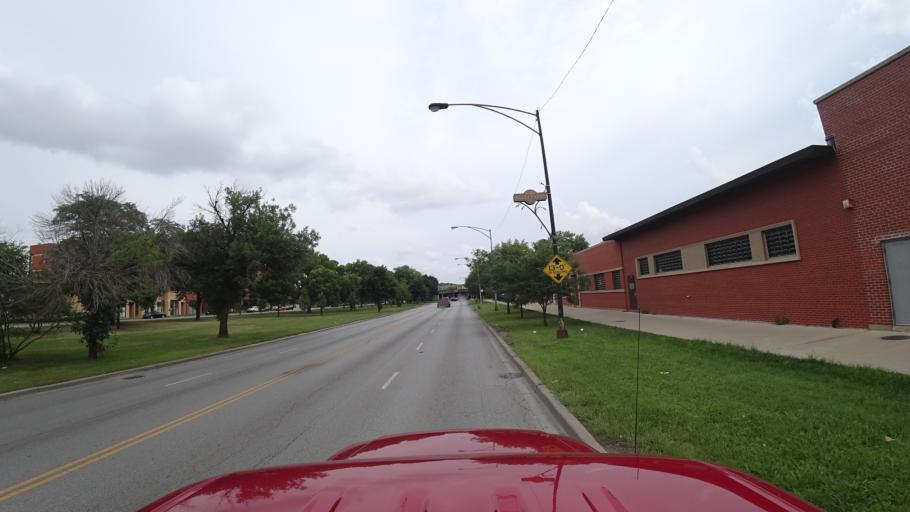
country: US
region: Illinois
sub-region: Cook County
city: Chicago
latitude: 41.8198
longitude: -87.6841
